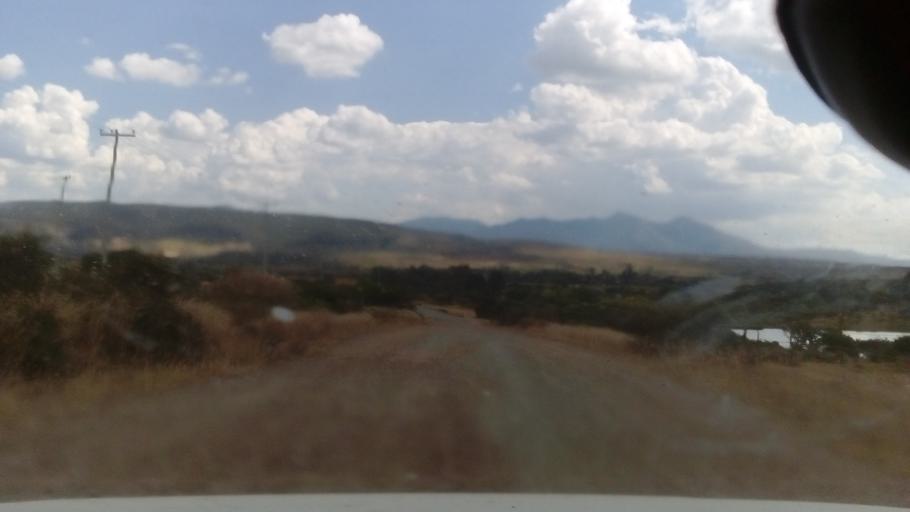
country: MX
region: Guanajuato
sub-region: Silao de la Victoria
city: San Francisco (Banos de Agua Caliente)
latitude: 21.1994
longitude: -101.4460
